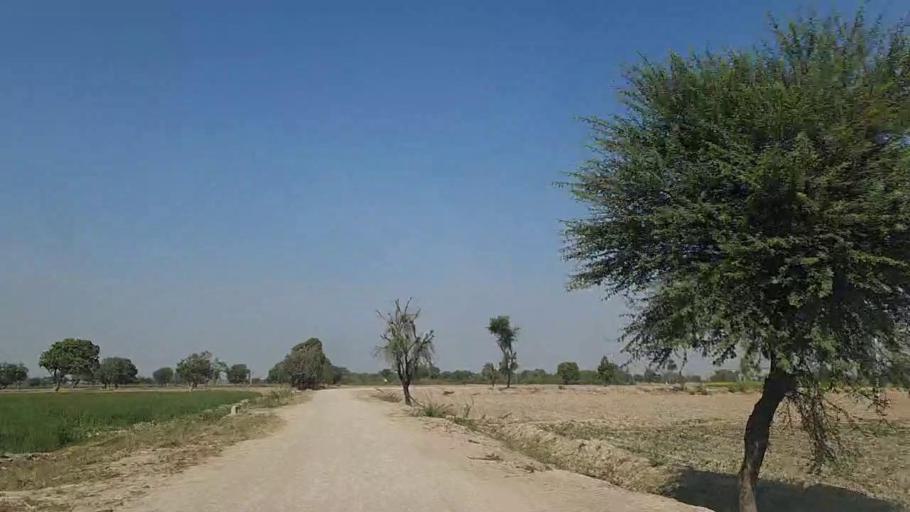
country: PK
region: Sindh
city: Naukot
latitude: 24.8561
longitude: 69.4156
